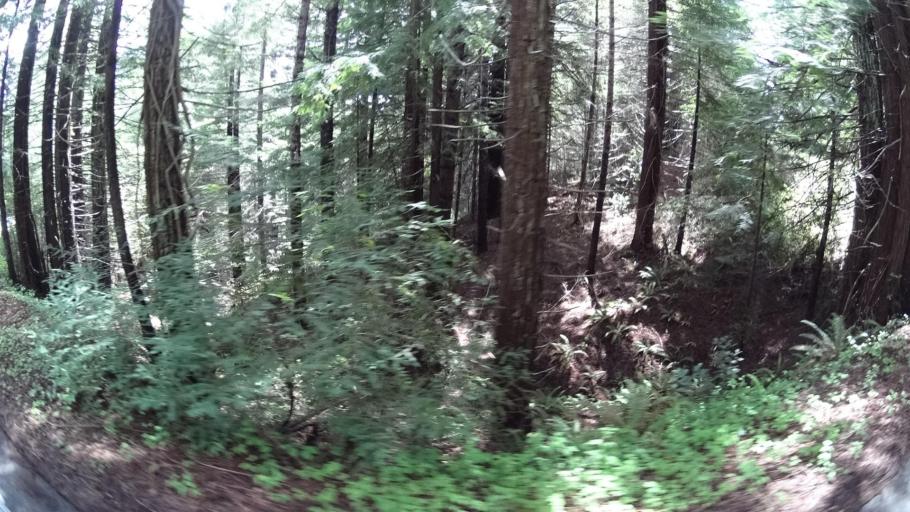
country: US
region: California
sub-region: Humboldt County
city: Blue Lake
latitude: 40.8439
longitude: -123.8998
